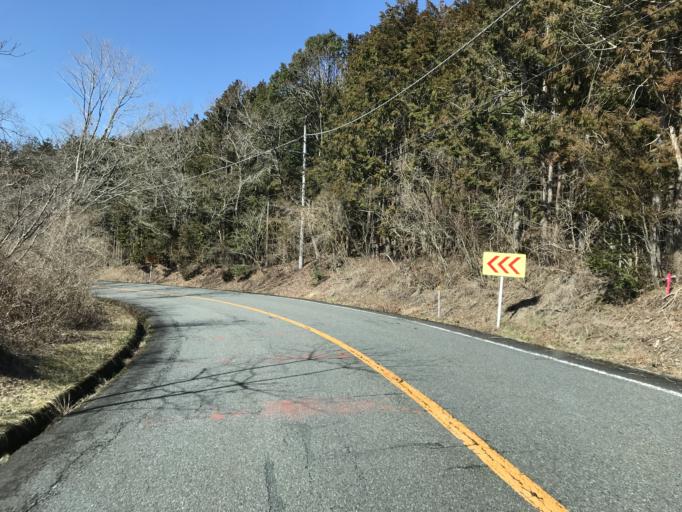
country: JP
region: Shizuoka
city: Fujinomiya
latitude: 35.2935
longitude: 138.6635
